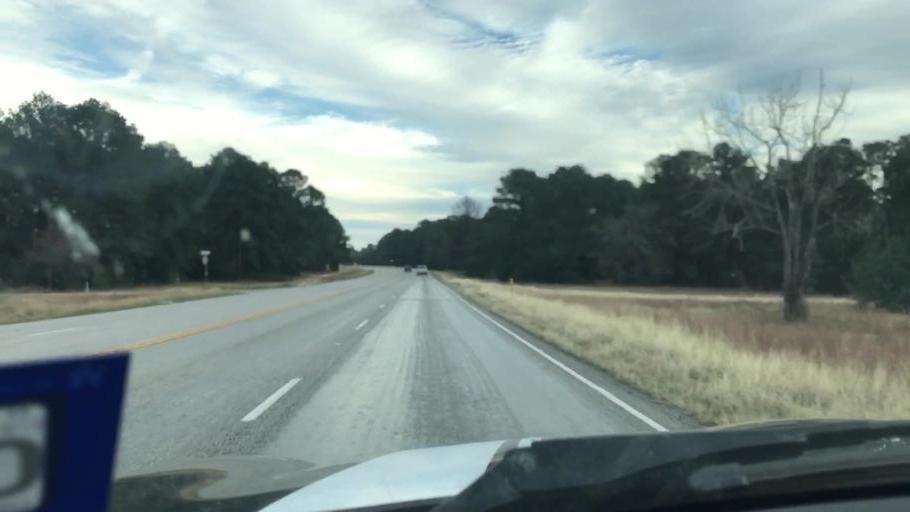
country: US
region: Texas
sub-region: Bastrop County
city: Camp Swift
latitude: 30.2431
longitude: -97.2159
